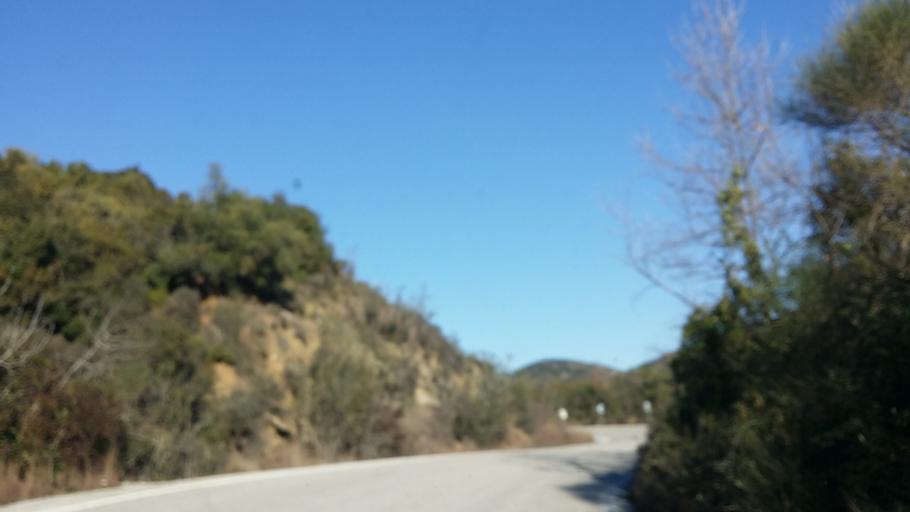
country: GR
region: West Greece
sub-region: Nomos Aitolias kai Akarnanias
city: Lepenou
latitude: 38.7675
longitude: 21.3367
